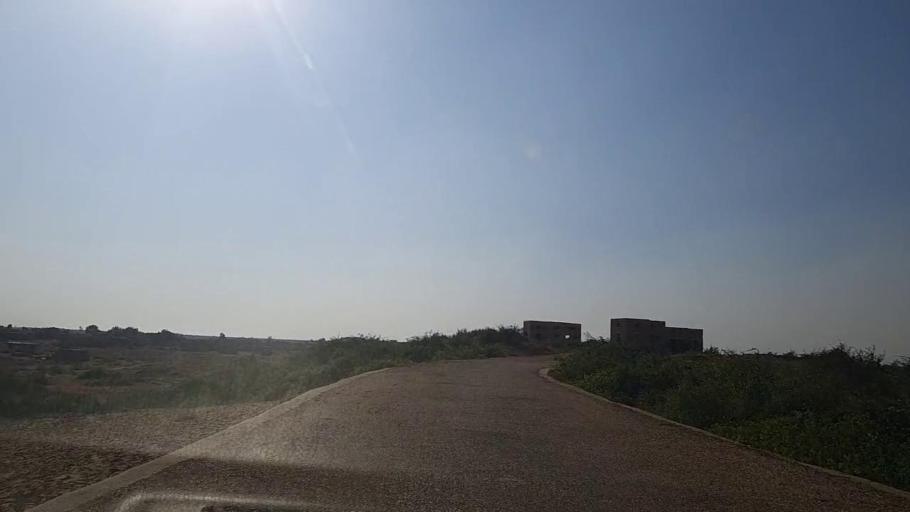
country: PK
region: Sindh
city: Daro Mehar
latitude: 25.0065
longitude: 68.1198
